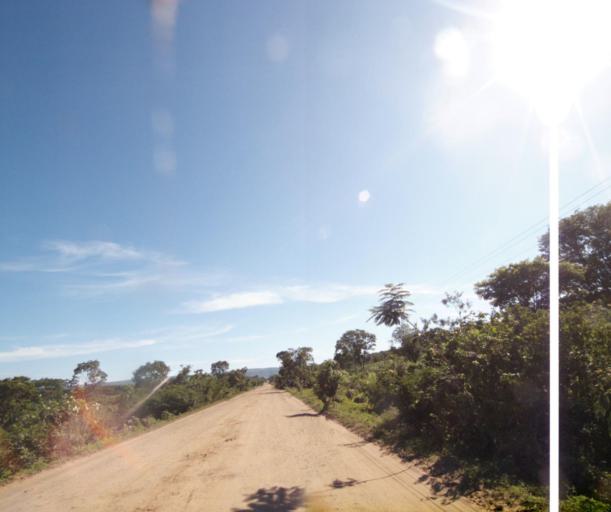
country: BR
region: Bahia
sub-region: Sao Felix Do Coribe
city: Santa Maria da Vitoria
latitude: -13.6348
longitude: -44.4319
